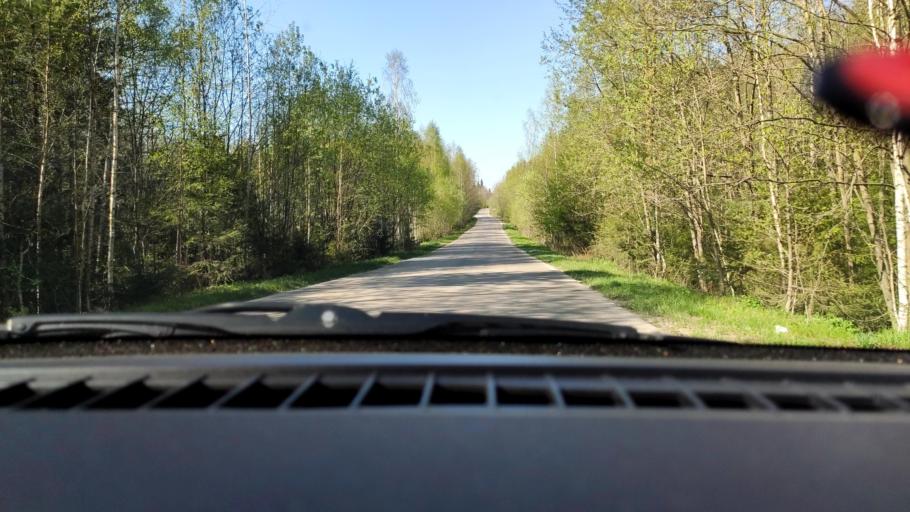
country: RU
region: Perm
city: Overyata
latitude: 58.0684
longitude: 56.0017
